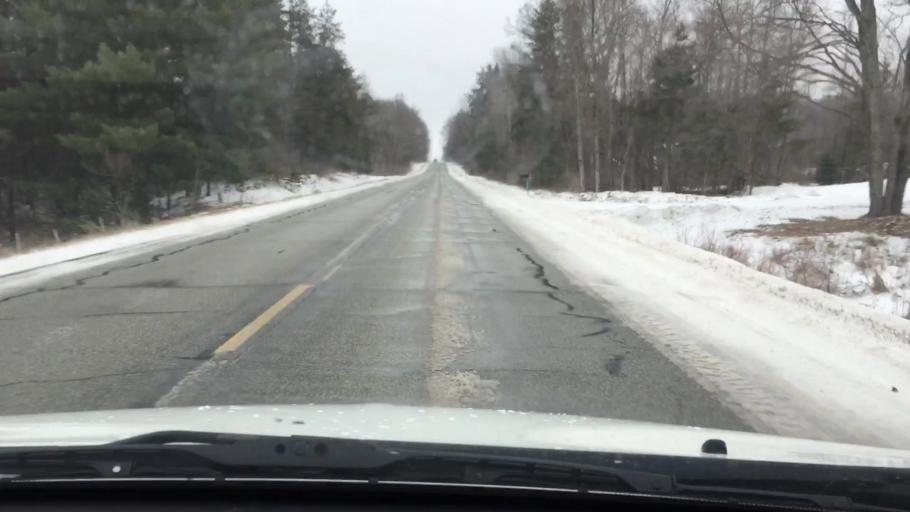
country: US
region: Michigan
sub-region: Wexford County
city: Cadillac
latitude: 44.1875
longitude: -85.4056
